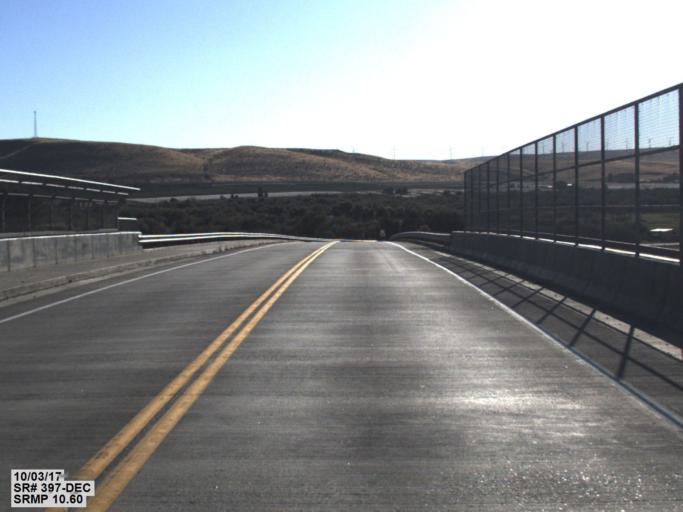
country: US
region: Washington
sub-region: Benton County
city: Finley
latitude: 46.1410
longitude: -119.0144
